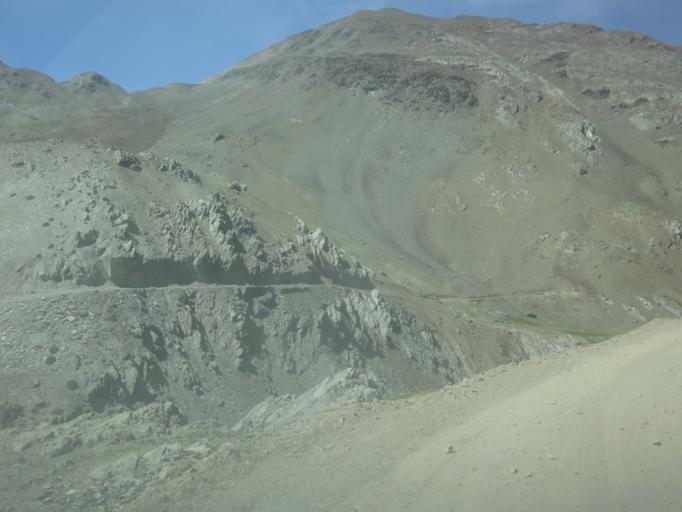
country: IN
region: Himachal Pradesh
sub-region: Kulu
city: Manali
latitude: 32.4216
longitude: 77.6515
